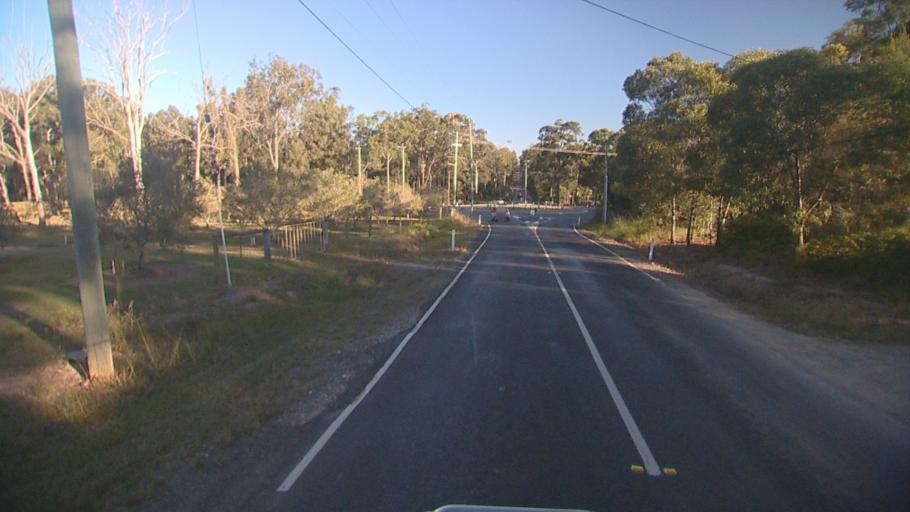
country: AU
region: Queensland
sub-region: Logan
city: Chambers Flat
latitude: -27.7695
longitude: 153.1377
